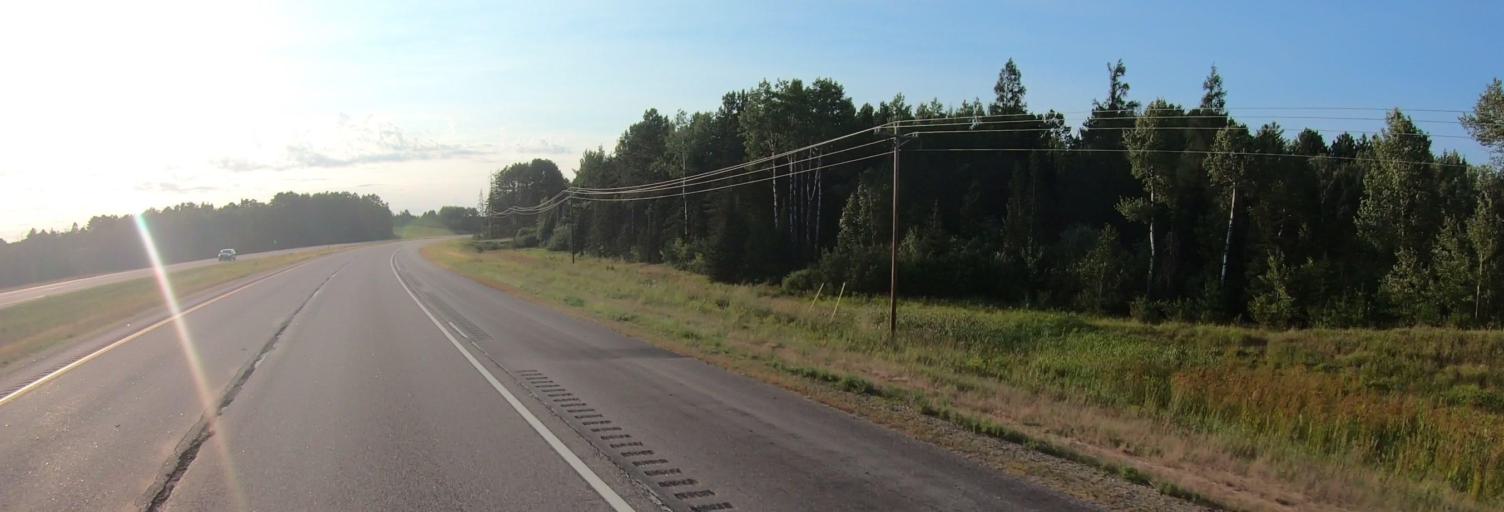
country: US
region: Minnesota
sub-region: Saint Louis County
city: Mountain Iron
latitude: 47.6694
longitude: -92.6306
